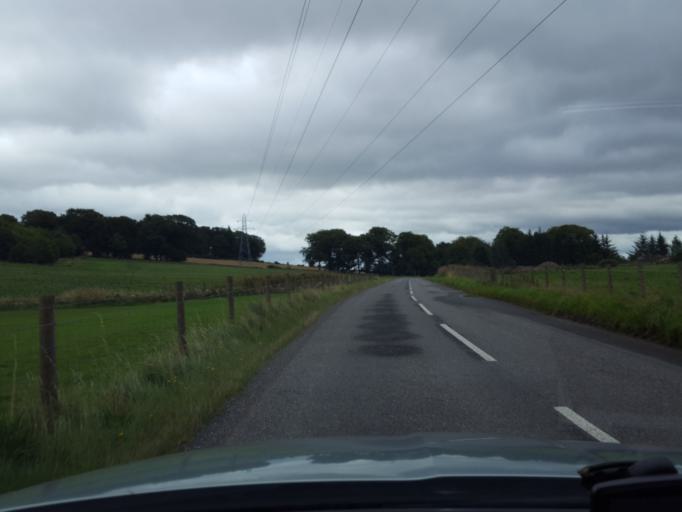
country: GB
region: Scotland
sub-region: Aberdeenshire
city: Banchory
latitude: 57.1476
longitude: -2.5072
